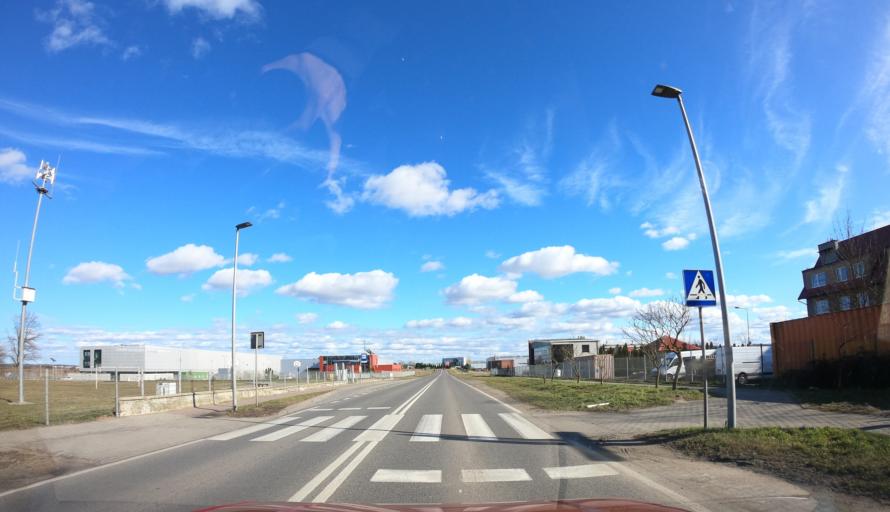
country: PL
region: West Pomeranian Voivodeship
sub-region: Powiat policki
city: Dobra
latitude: 53.4345
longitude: 14.4288
